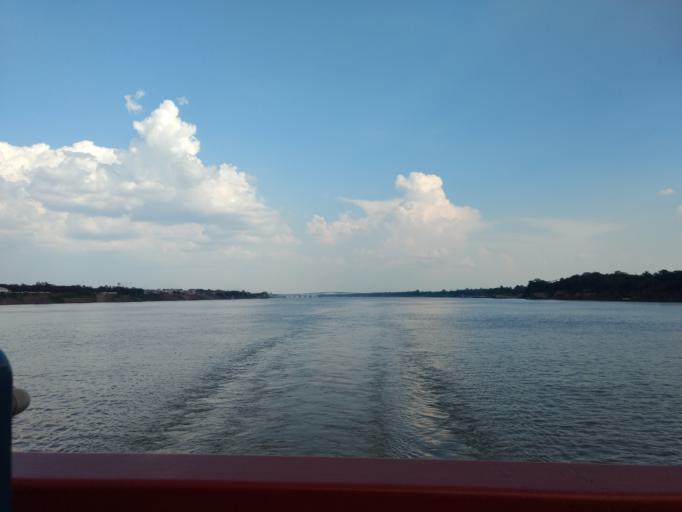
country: BR
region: Rondonia
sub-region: Porto Velho
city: Porto Velho
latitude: -8.6963
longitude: -63.9223
